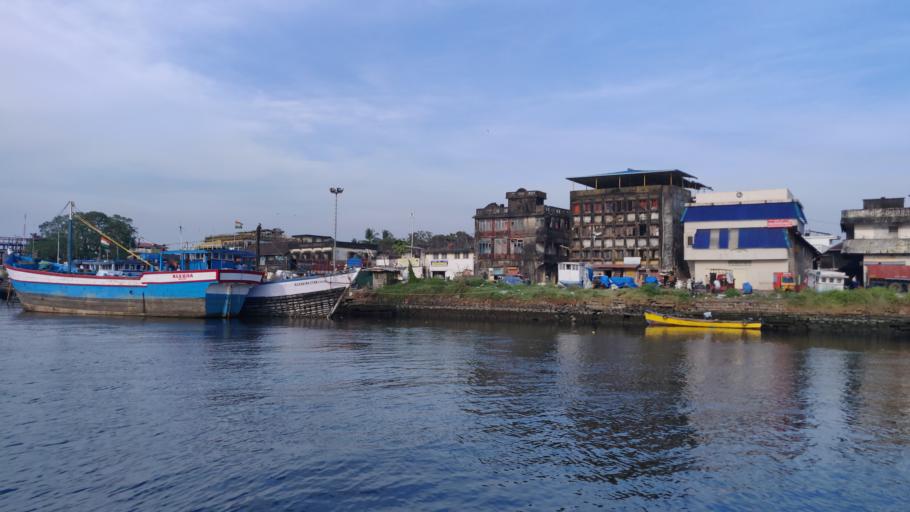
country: IN
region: Karnataka
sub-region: Dakshina Kannada
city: Mangalore
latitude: 12.8636
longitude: 74.8307
